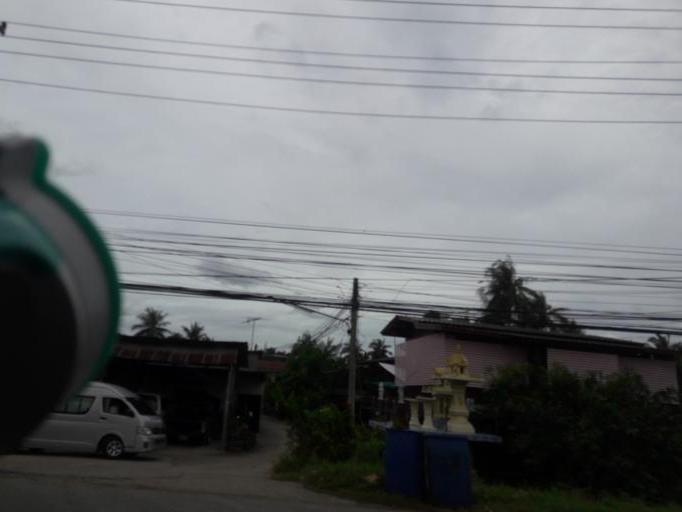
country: TH
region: Ratchaburi
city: Damnoen Saduak
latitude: 13.5181
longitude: 99.9726
